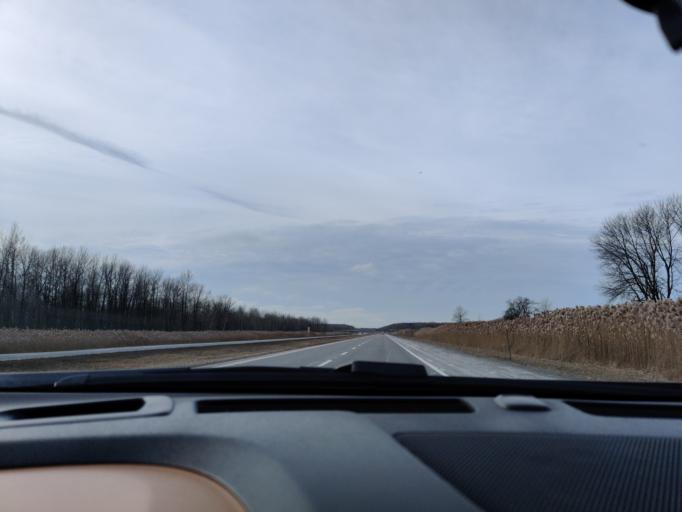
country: CA
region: Quebec
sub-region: Monteregie
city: Les Coteaux
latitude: 45.2397
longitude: -74.2795
